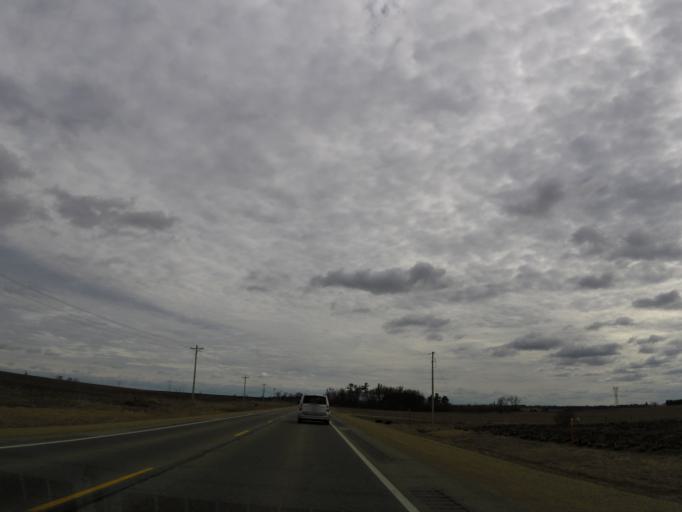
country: US
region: Iowa
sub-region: Chickasaw County
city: New Hampton
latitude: 43.1202
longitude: -92.2980
